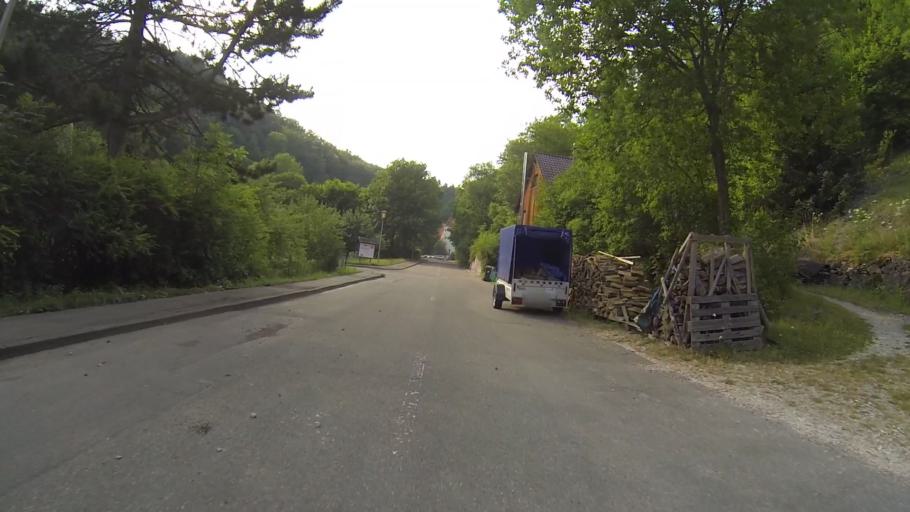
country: DE
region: Baden-Wuerttemberg
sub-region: Tuebingen Region
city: Dornstadt
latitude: 48.4460
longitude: 9.8637
